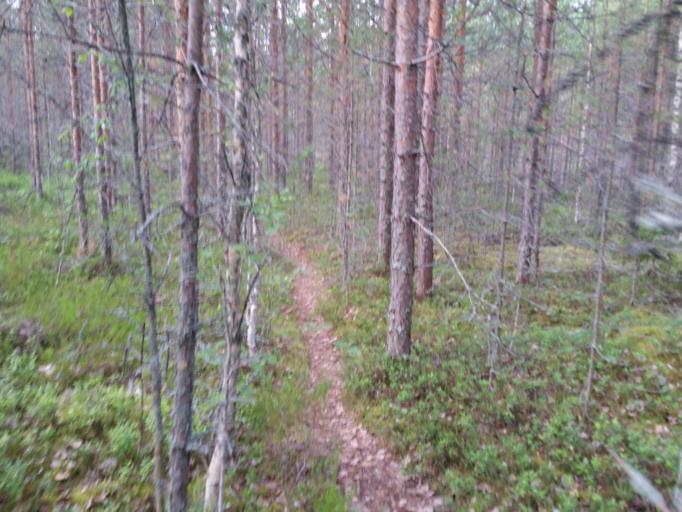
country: FI
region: Southern Savonia
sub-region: Savonlinna
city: Sulkava
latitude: 61.7642
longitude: 28.4340
